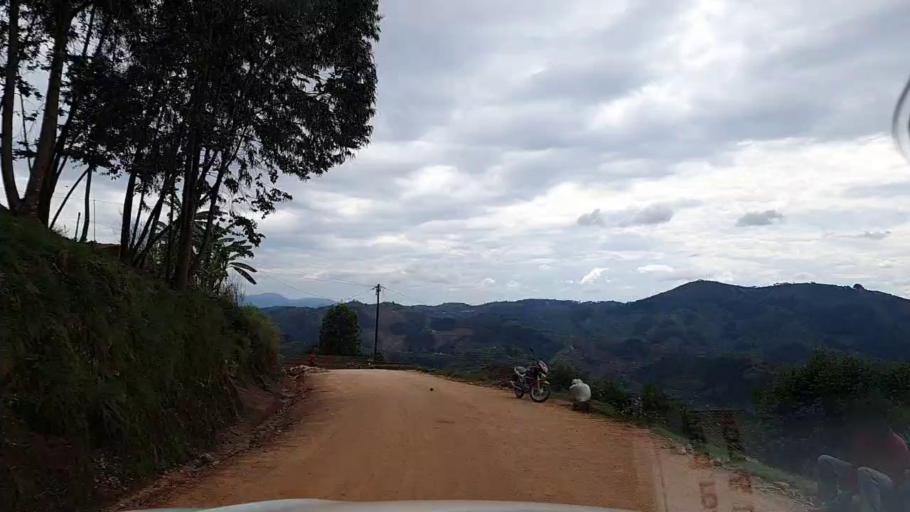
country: RW
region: Southern Province
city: Nzega
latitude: -2.4014
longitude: 29.4536
